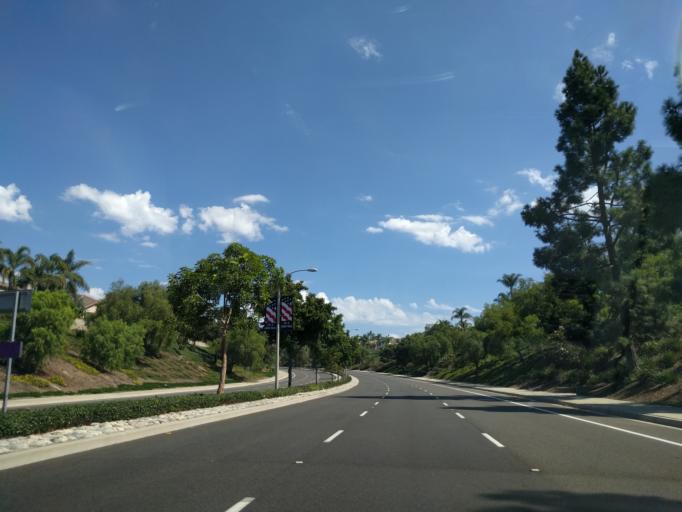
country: US
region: California
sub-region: Orange County
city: Dana Point
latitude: 33.4940
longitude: -117.6949
